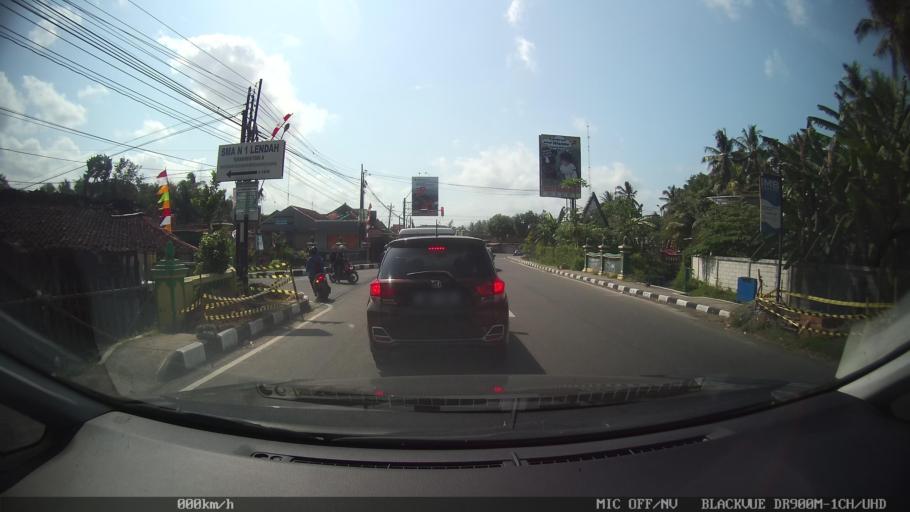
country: ID
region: Daerah Istimewa Yogyakarta
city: Srandakan
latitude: -7.9401
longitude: 110.2332
